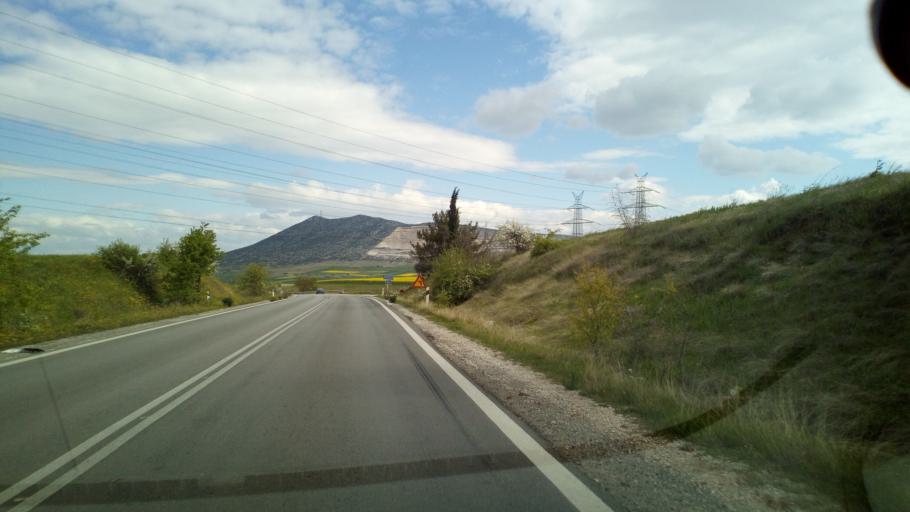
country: GR
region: Central Macedonia
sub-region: Nomos Thessalonikis
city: Drymos
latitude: 40.7951
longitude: 22.9479
